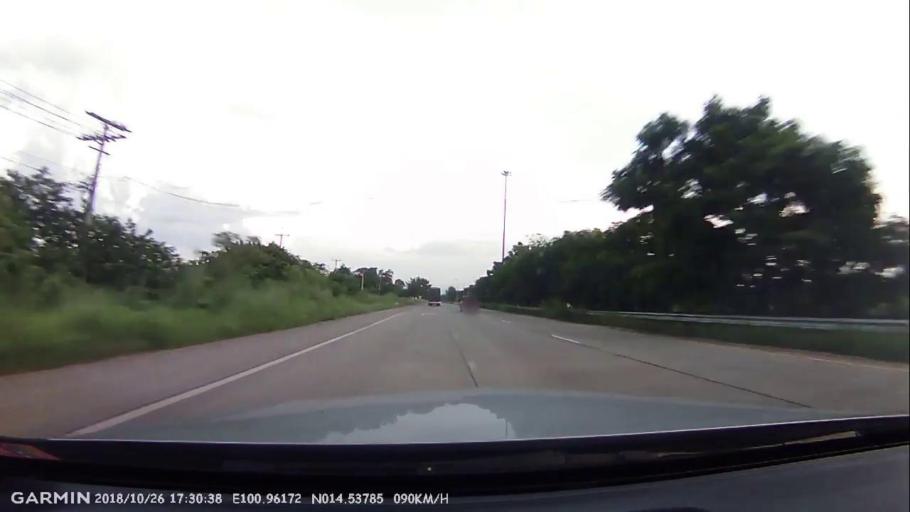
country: TH
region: Sara Buri
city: Saraburi
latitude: 14.5377
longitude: 100.9620
